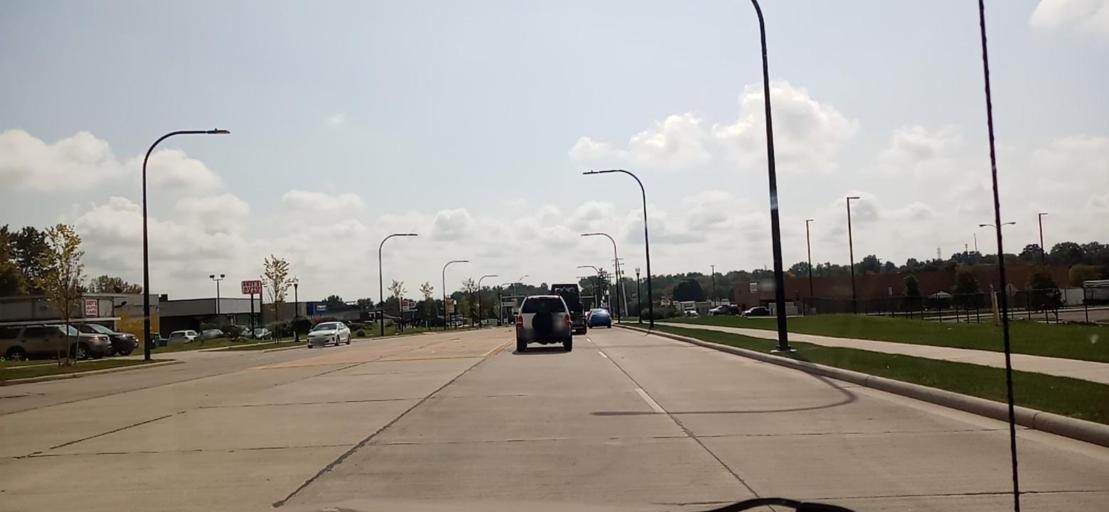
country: US
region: Ohio
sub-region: Summit County
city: Barberton
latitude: 41.0483
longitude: -81.5809
